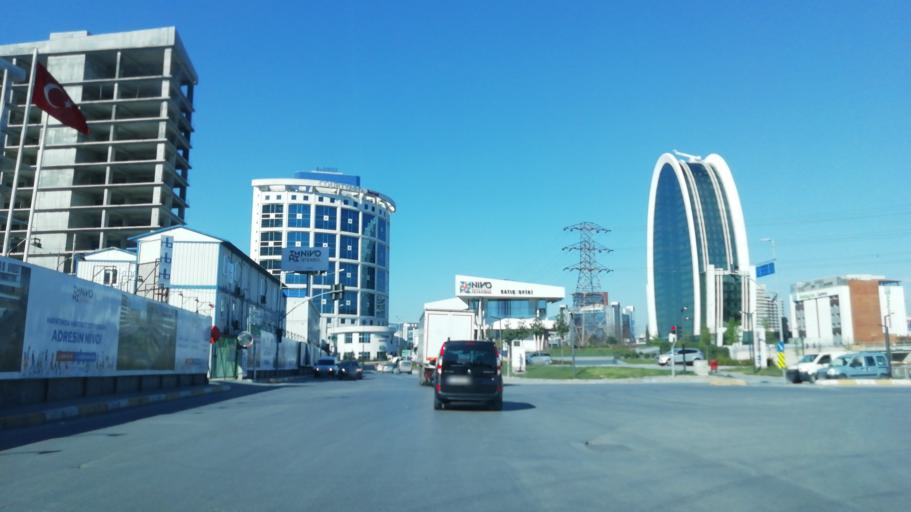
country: TR
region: Istanbul
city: Mahmutbey
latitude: 41.0267
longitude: 28.8074
